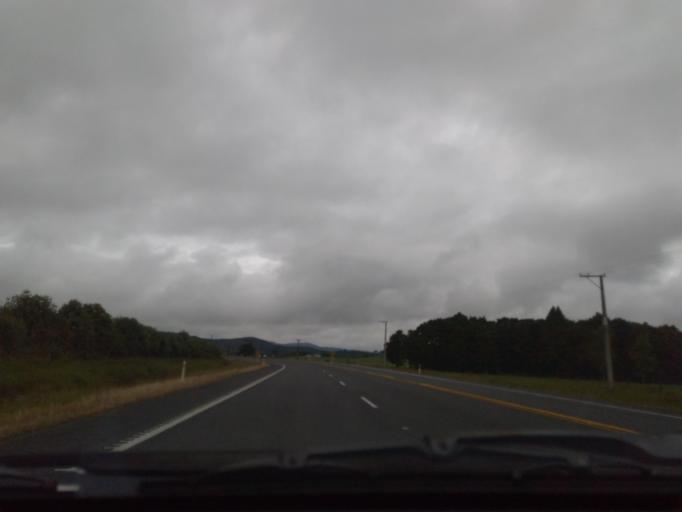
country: NZ
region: Northland
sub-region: Whangarei
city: Ruakaka
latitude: -36.0114
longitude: 174.4180
